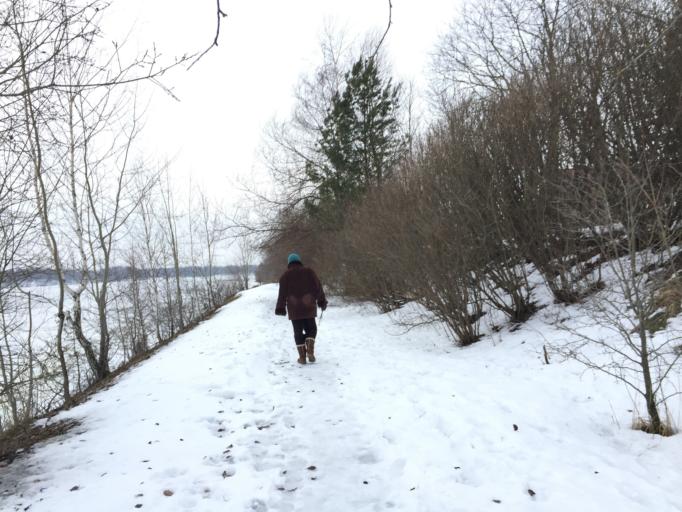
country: LV
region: Ikskile
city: Ikskile
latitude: 56.8427
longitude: 24.4347
